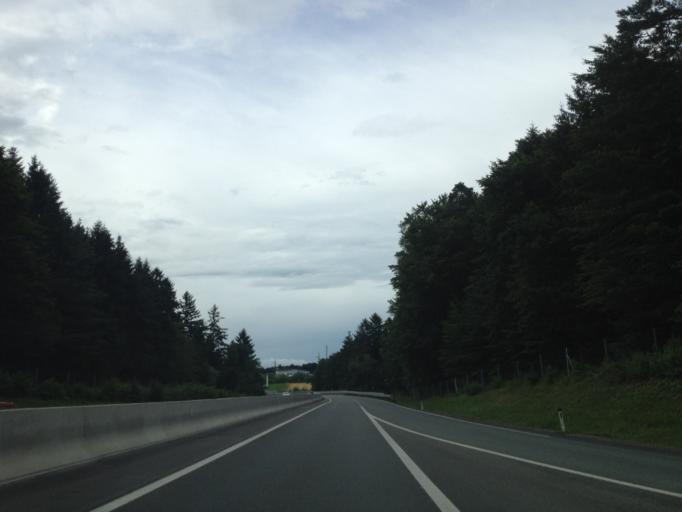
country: AT
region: Styria
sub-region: Politischer Bezirk Hartberg-Fuerstenfeld
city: Sankt Johann in der Haide
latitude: 47.2757
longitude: 16.0105
